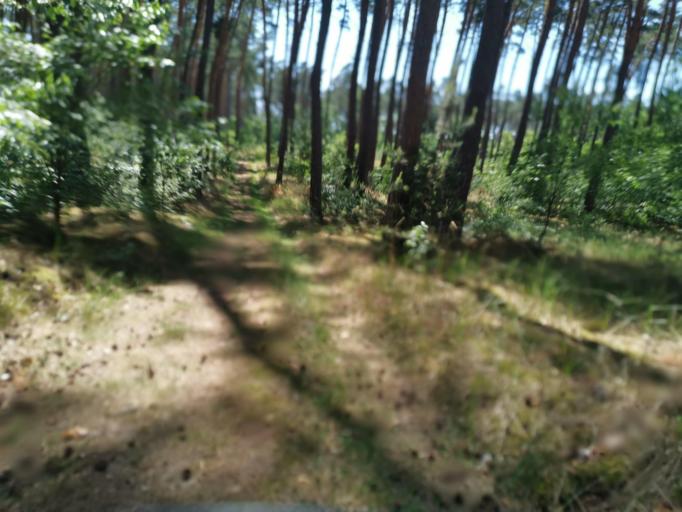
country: CZ
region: South Moravian
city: Rohatec
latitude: 48.9104
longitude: 17.2201
